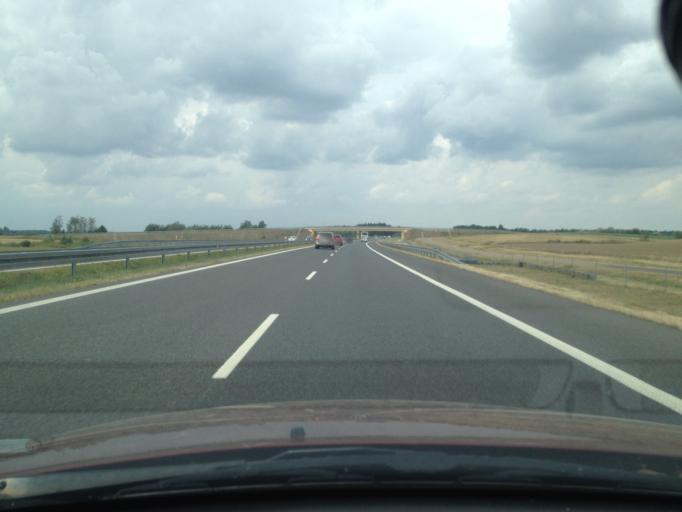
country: PL
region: West Pomeranian Voivodeship
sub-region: Powiat pyrzycki
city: Lipiany
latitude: 52.9569
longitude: 14.9353
